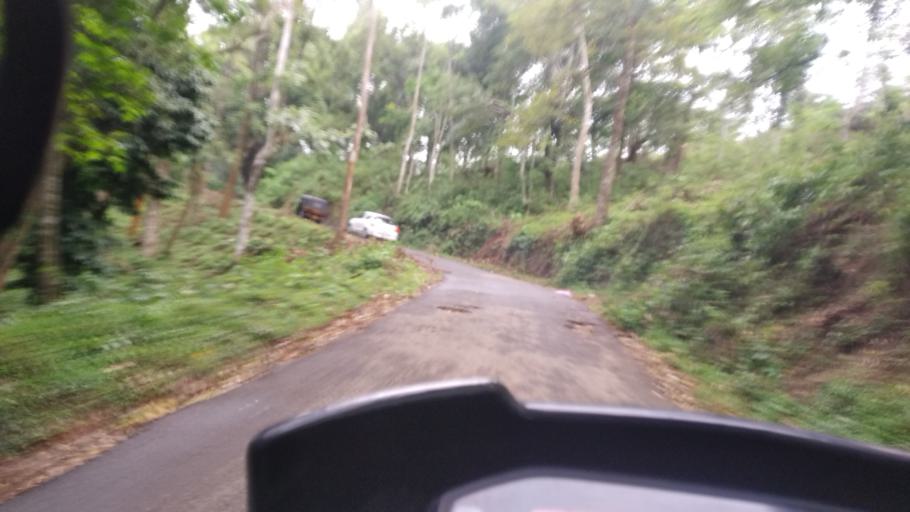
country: IN
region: Tamil Nadu
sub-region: Theni
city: Gudalur
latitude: 9.5505
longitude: 77.0581
